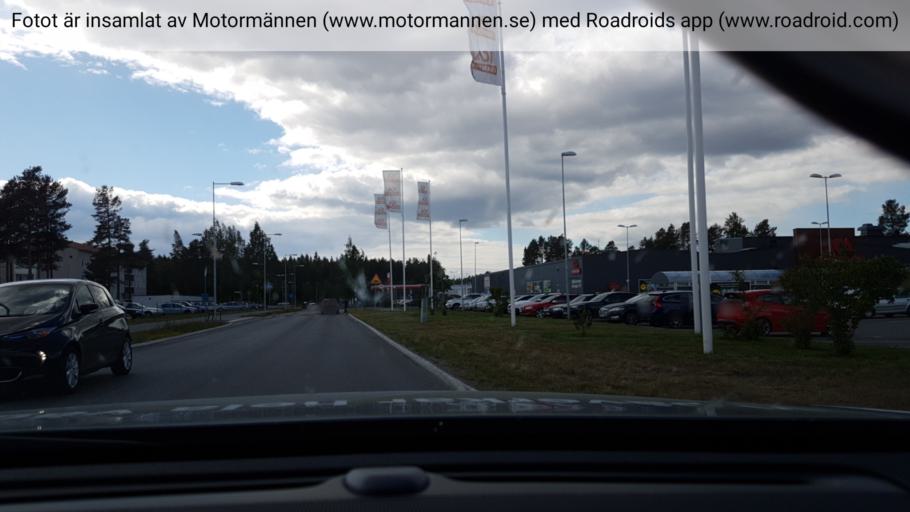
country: SE
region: Vaesterbotten
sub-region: Umea Kommun
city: Roback
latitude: 63.8399
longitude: 20.1940
